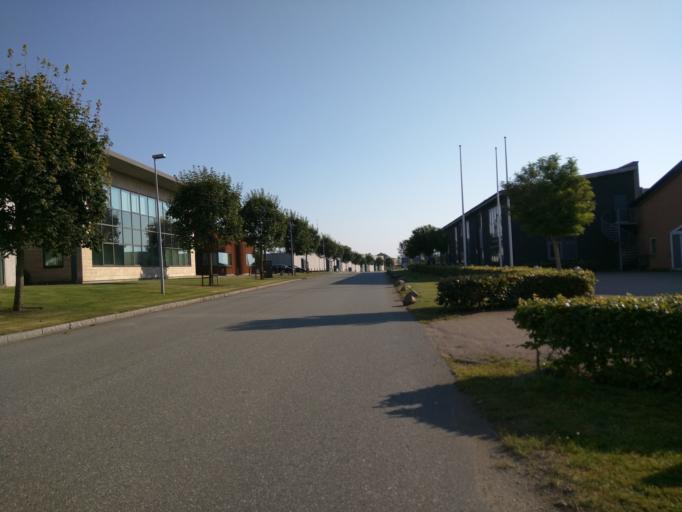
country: DK
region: Central Jutland
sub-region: Viborg Kommune
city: Viborg
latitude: 56.4516
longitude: 9.3583
